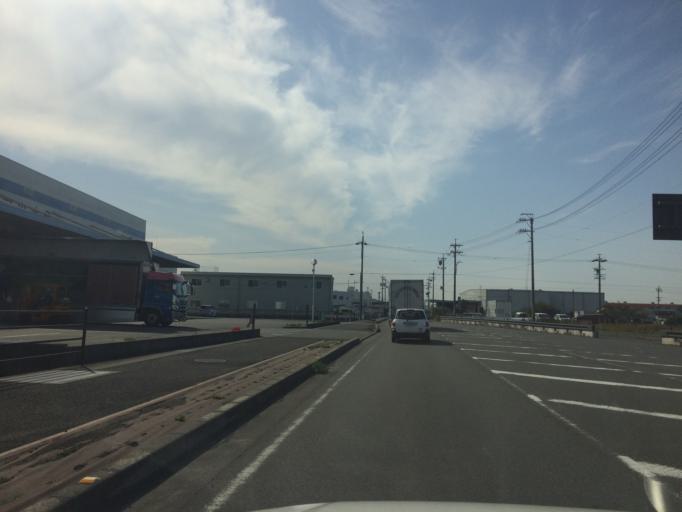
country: JP
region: Shizuoka
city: Fujieda
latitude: 34.7863
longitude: 138.2901
